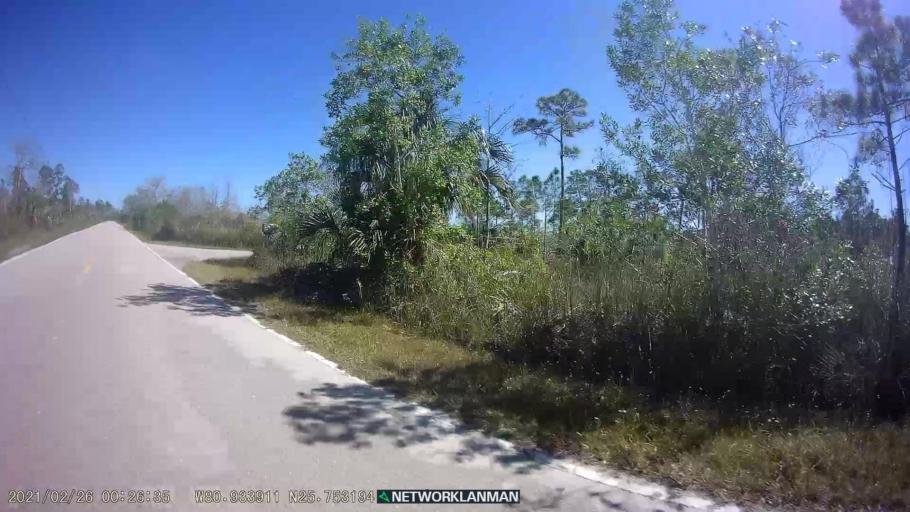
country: US
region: Florida
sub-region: Miami-Dade County
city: The Hammocks
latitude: 25.7535
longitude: -80.9341
